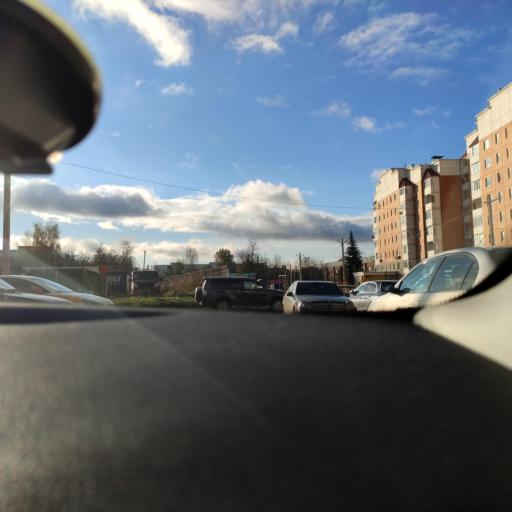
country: RU
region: Moskovskaya
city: Shcherbinka
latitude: 55.4741
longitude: 37.6088
